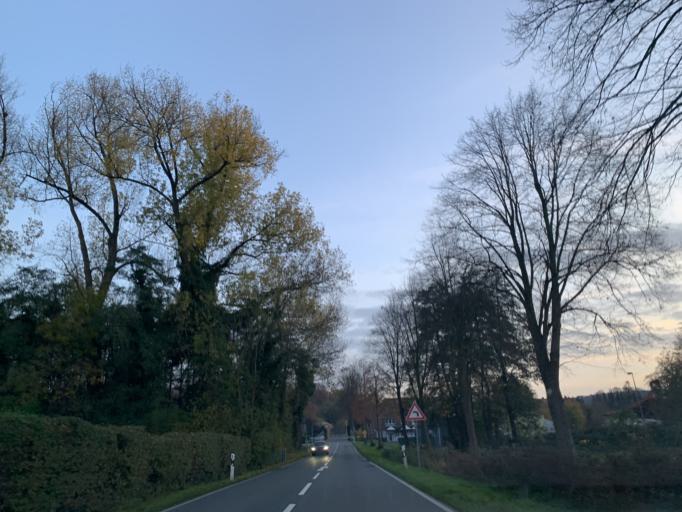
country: DE
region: North Rhine-Westphalia
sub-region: Regierungsbezirk Munster
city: Havixbeck
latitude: 51.9690
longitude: 7.4077
